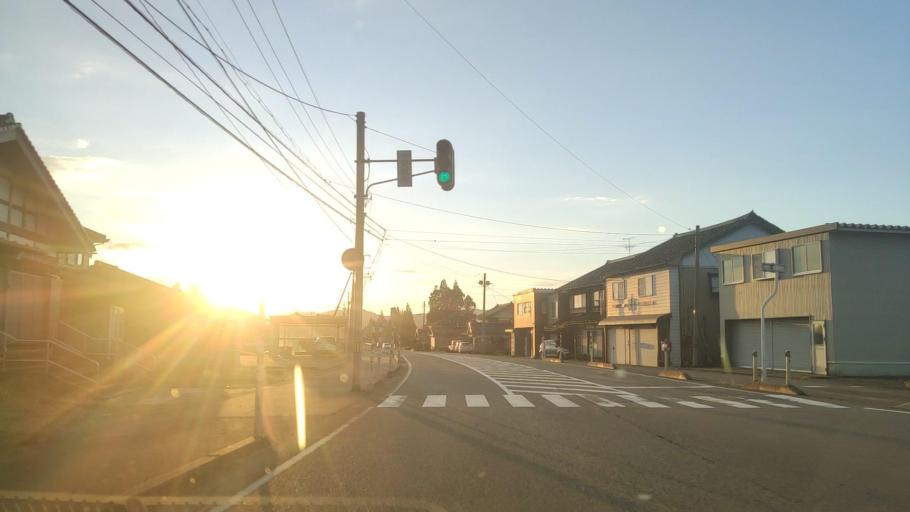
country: JP
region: Toyama
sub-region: Oyabe Shi
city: Oyabe
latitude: 36.6312
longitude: 136.8706
